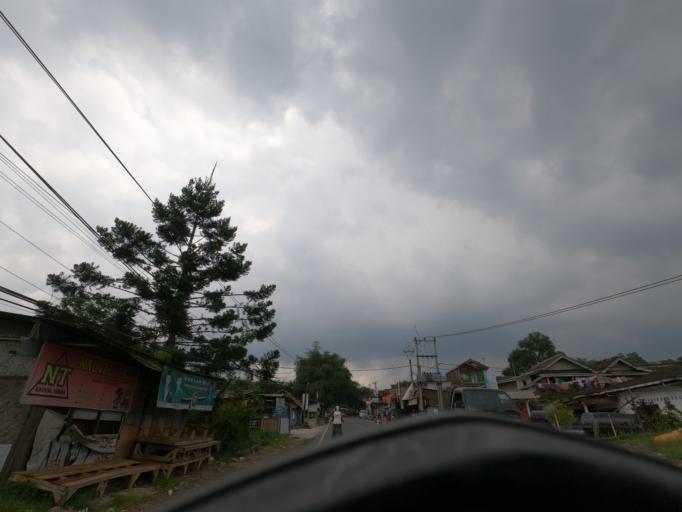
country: ID
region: West Java
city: Sukabumi
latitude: -6.7814
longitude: 107.0631
